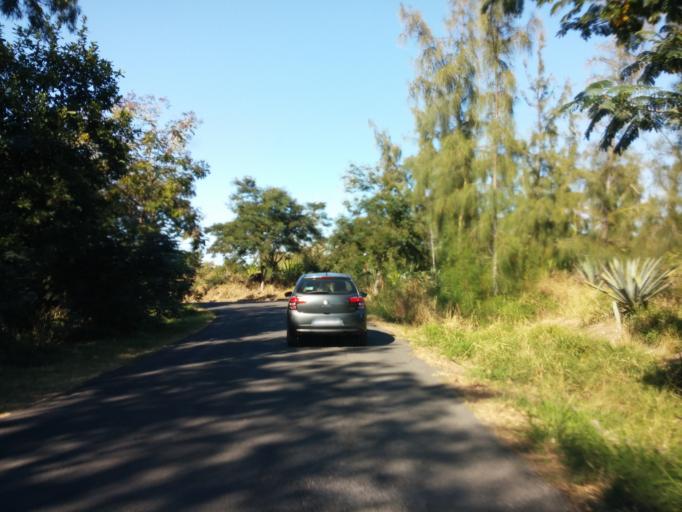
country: RE
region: Reunion
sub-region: Reunion
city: Les Avirons
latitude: -21.2730
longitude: 55.3539
